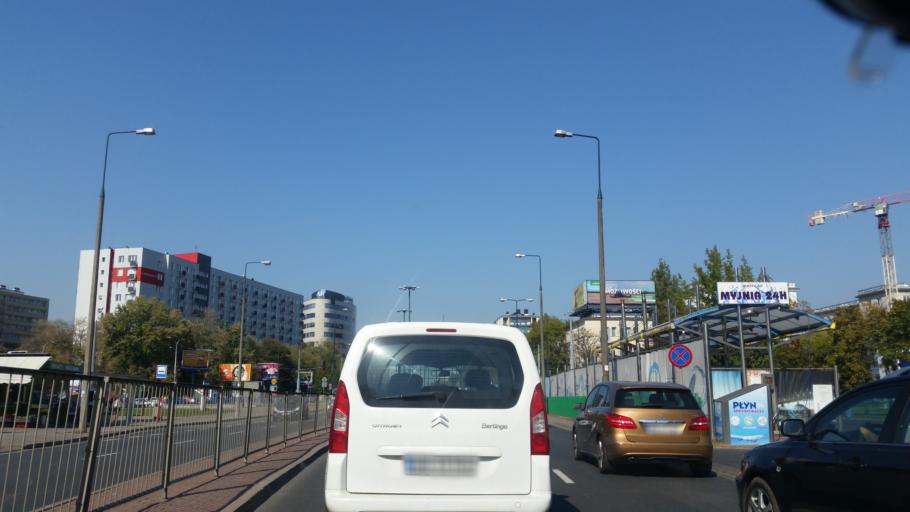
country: PL
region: Masovian Voivodeship
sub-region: Warszawa
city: Mokotow
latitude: 52.1882
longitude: 21.0176
